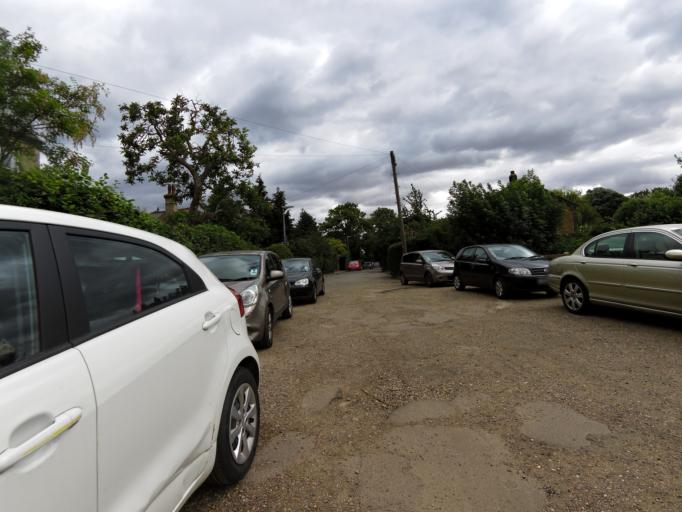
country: GB
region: England
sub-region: Cambridgeshire
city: Cambridge
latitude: 52.1927
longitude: 0.1062
